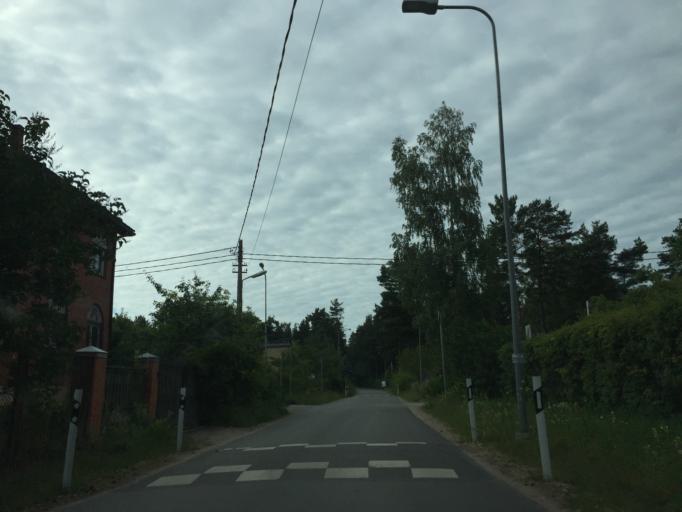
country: LV
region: Carnikava
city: Carnikava
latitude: 57.1324
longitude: 24.2525
